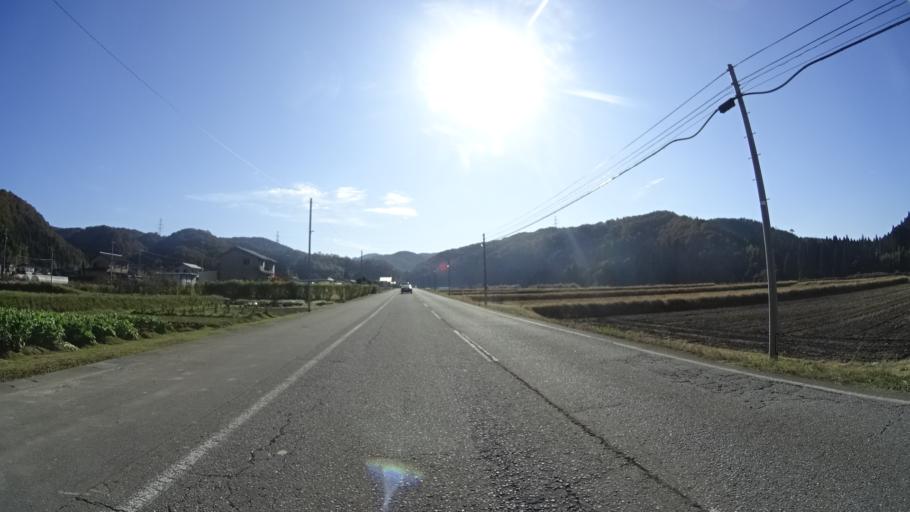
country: JP
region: Ishikawa
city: Komatsu
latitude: 36.3826
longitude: 136.5331
